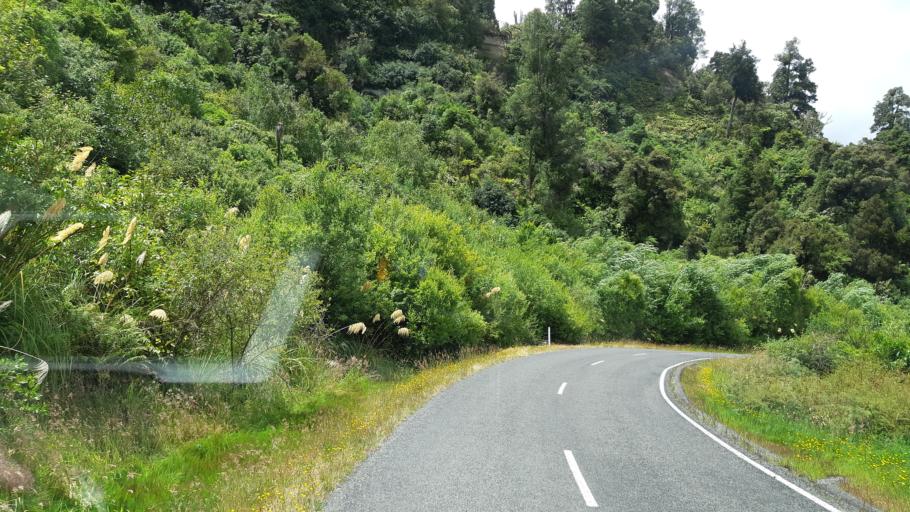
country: NZ
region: Manawatu-Wanganui
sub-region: Ruapehu District
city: Waiouru
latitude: -39.9350
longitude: 175.9255
